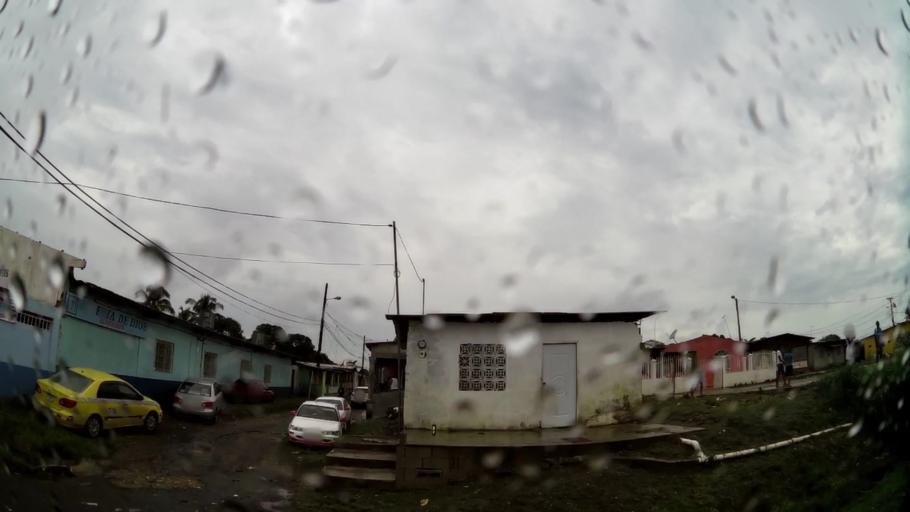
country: PA
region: Colon
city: Arco Iris
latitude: 9.3375
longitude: -79.8666
